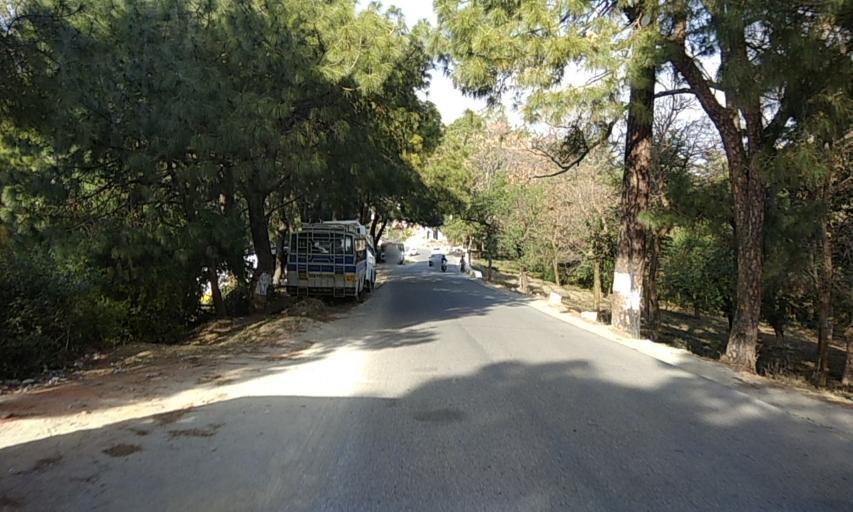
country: IN
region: Himachal Pradesh
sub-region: Kangra
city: Palampur
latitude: 32.0973
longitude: 76.5314
